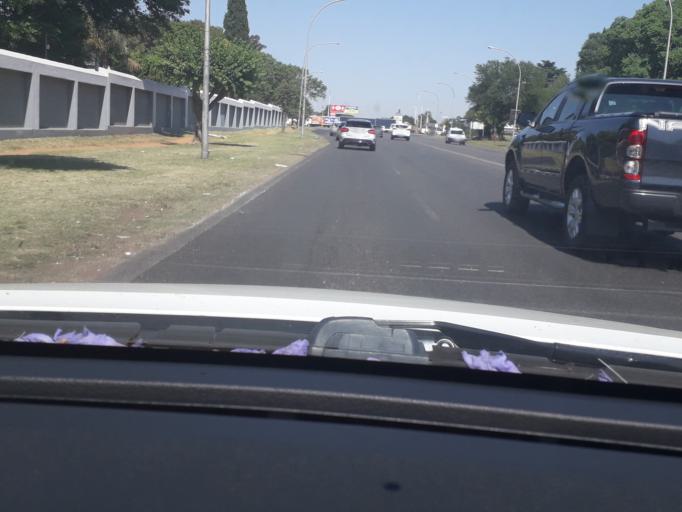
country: ZA
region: Gauteng
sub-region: Ekurhuleni Metropolitan Municipality
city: Benoni
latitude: -26.1794
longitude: 28.2832
